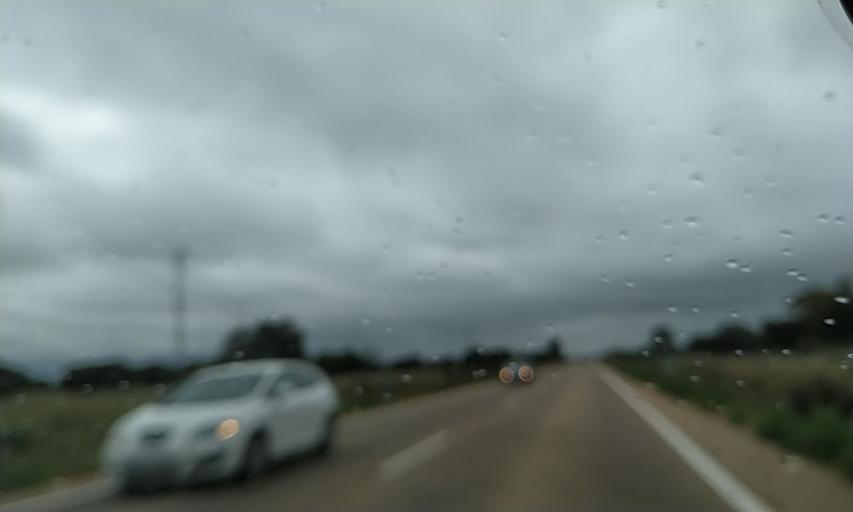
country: ES
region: Extremadura
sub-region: Provincia de Badajoz
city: Villar del Rey
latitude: 38.9913
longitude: -6.8743
